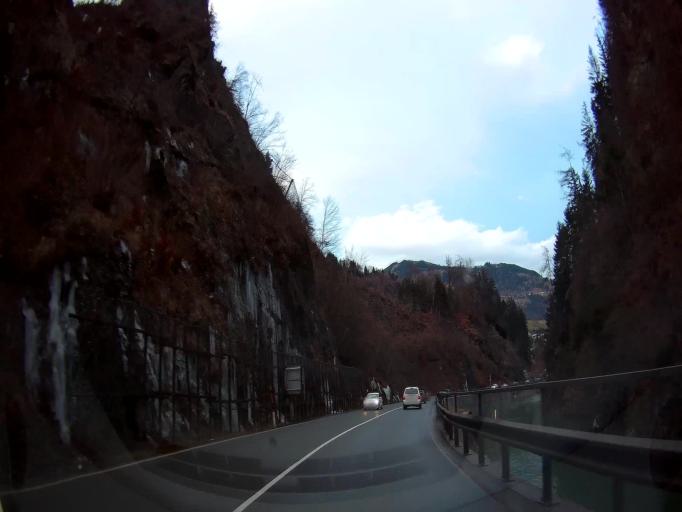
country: AT
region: Salzburg
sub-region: Politischer Bezirk Sankt Johann im Pongau
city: Schwarzach im Pongau
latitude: 47.3121
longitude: 13.1287
